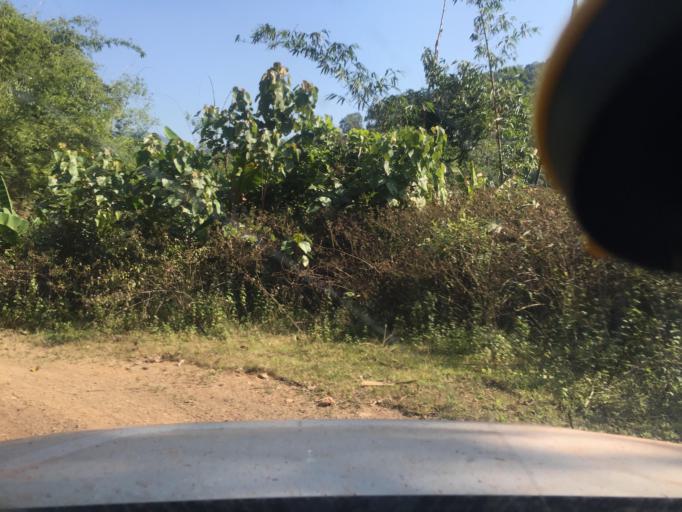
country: LA
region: Phongsali
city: Phongsali
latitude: 21.7021
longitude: 102.3918
